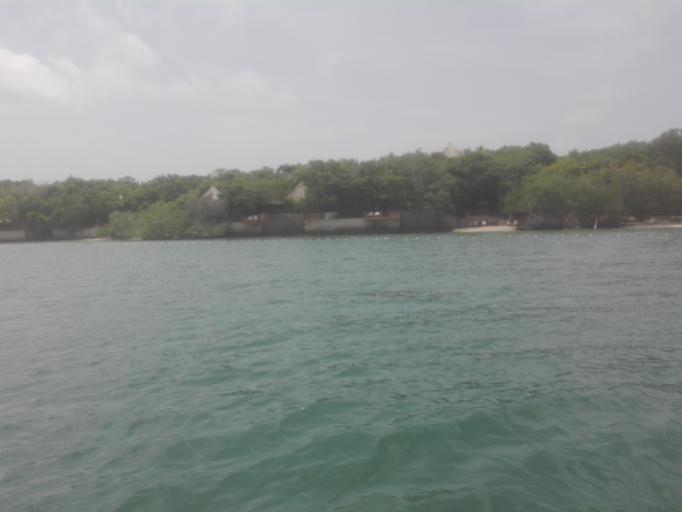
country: CO
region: Bolivar
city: Turbana
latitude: 10.1529
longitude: -75.6873
